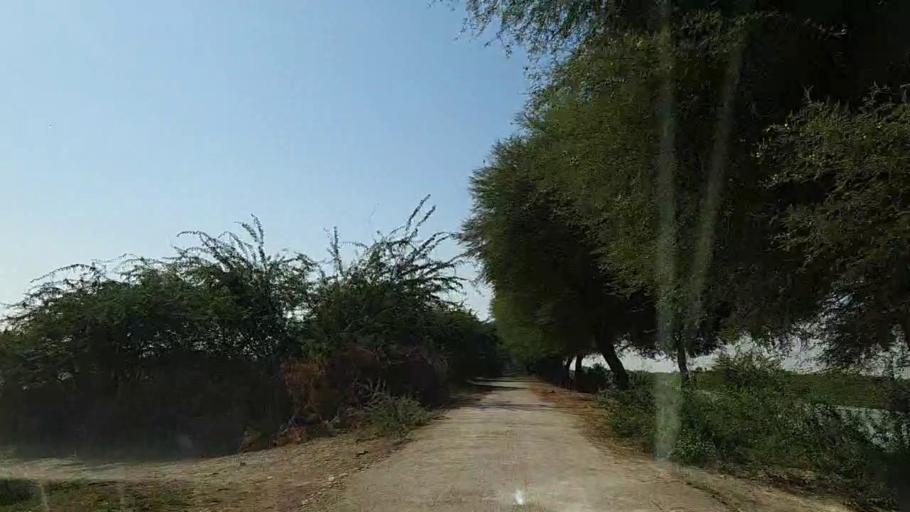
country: PK
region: Sindh
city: Chuhar Jamali
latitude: 24.5756
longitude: 68.0452
